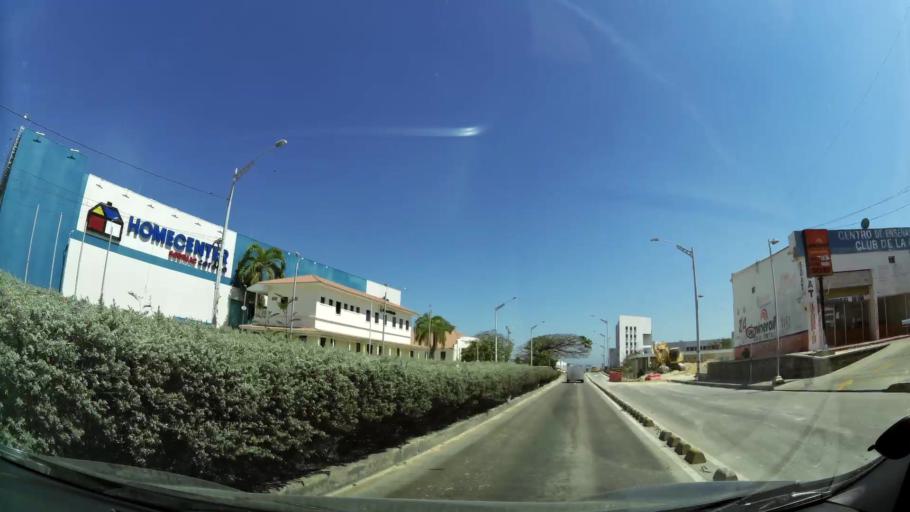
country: CO
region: Atlantico
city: Barranquilla
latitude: 10.9881
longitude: -74.7878
